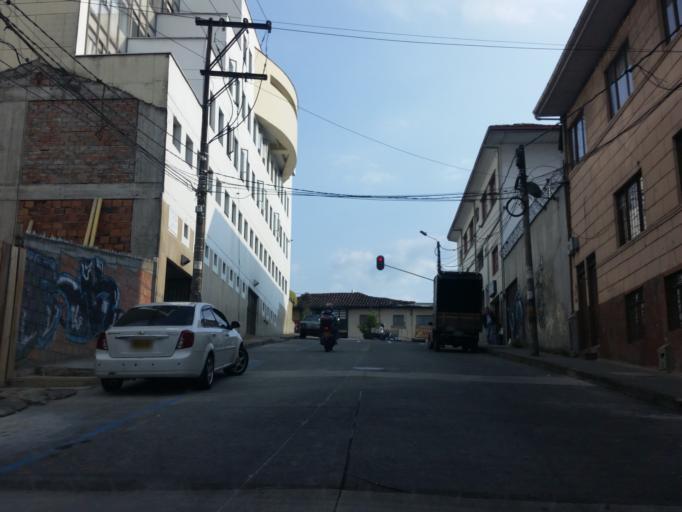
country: CO
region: Caldas
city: Manizales
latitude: 5.0662
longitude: -75.5020
